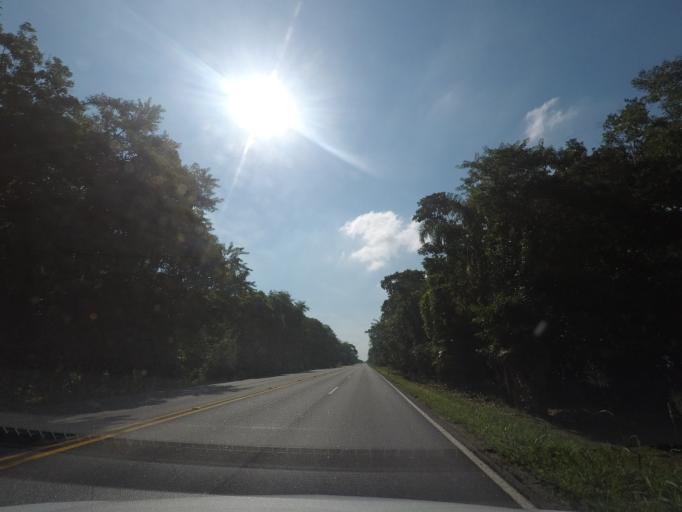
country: BR
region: Parana
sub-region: Pontal Do Parana
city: Pontal do Parana
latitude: -25.6436
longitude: -48.5904
